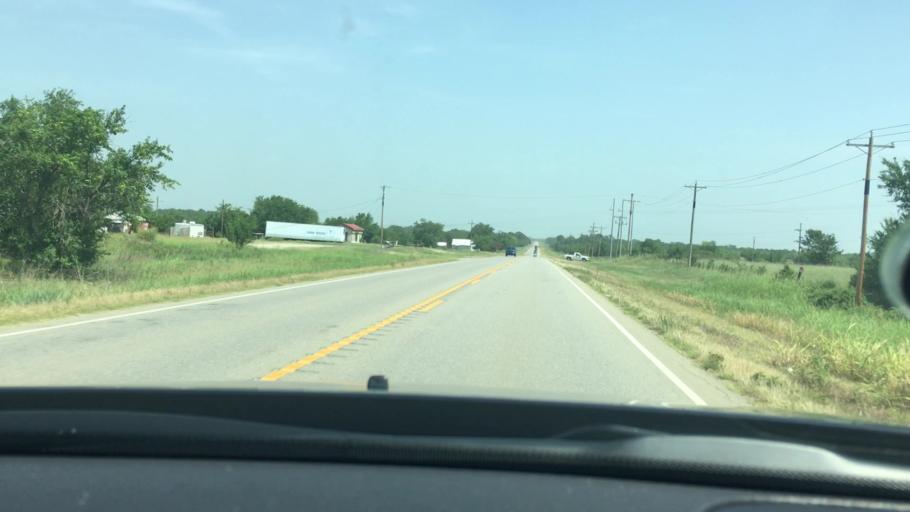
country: US
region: Oklahoma
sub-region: Coal County
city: Coalgate
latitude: 34.4823
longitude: -96.2183
